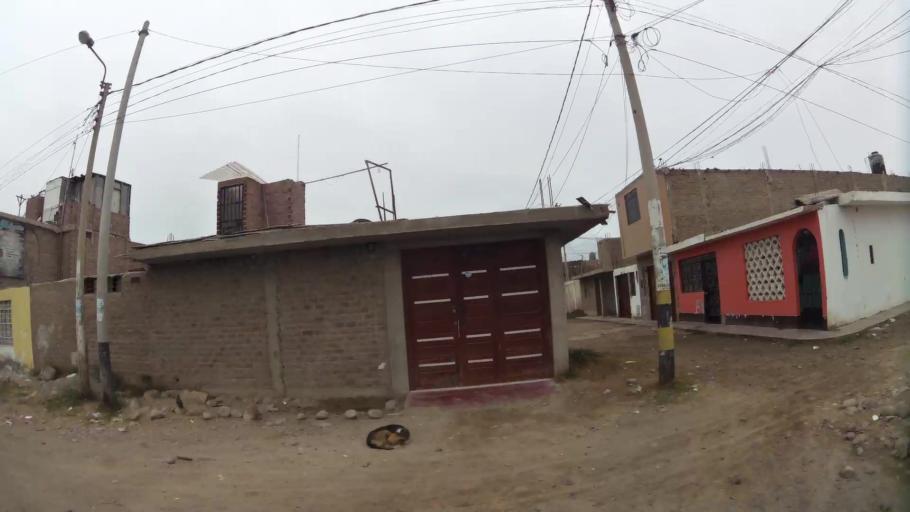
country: PE
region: Ica
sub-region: Provincia de Pisco
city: Pisco
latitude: -13.7187
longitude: -76.2126
